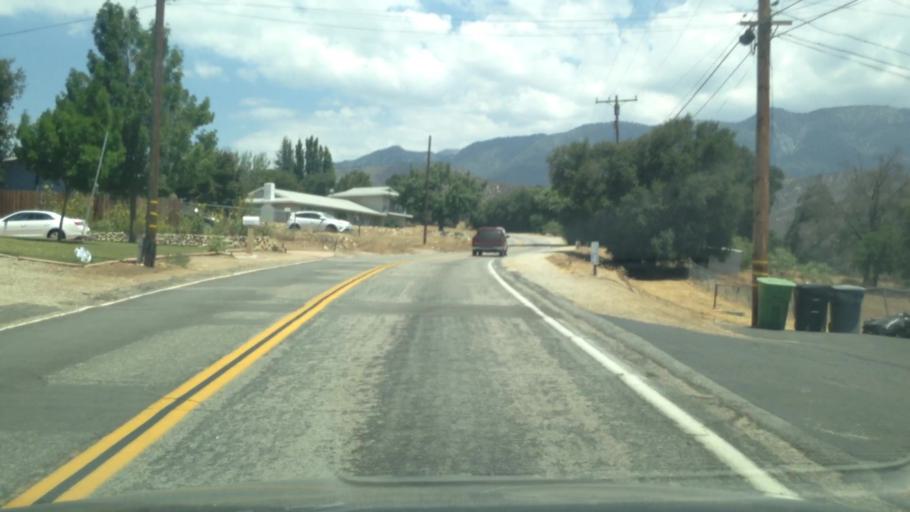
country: US
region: California
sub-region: Riverside County
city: Cherry Valley
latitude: 33.9971
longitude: -116.9627
